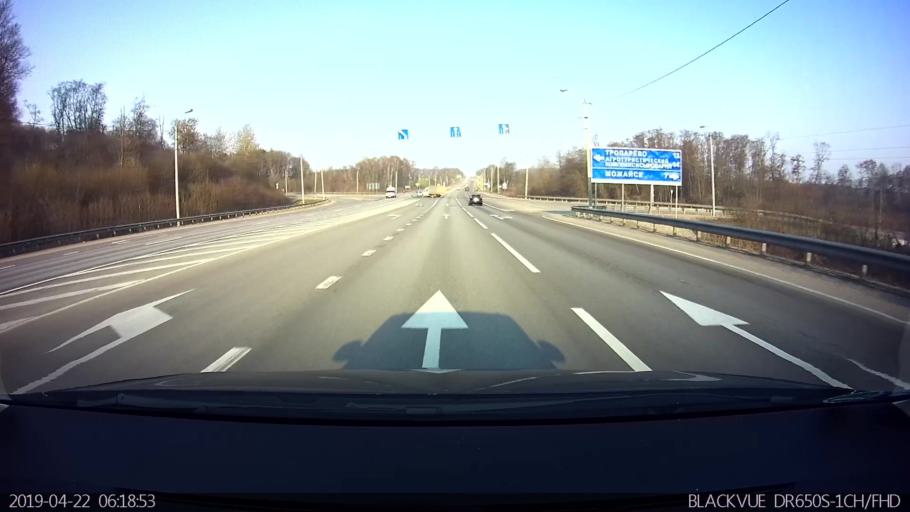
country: RU
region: Moskovskaya
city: Mozhaysk
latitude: 55.4640
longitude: 35.9450
